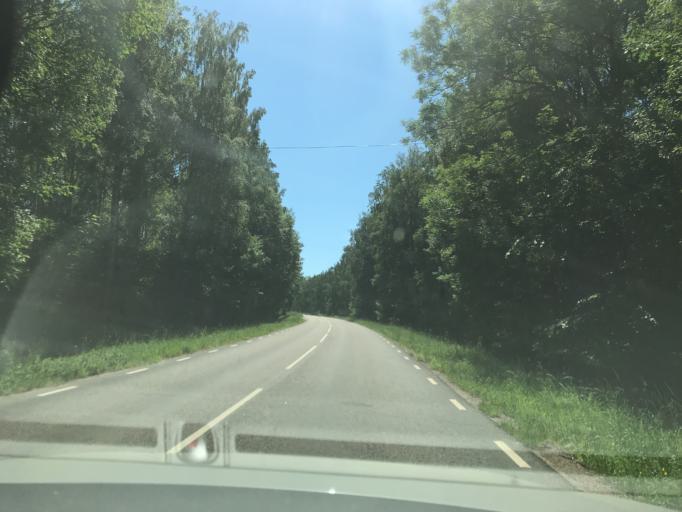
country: SE
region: Vaestra Goetaland
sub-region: Gotene Kommun
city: Goetene
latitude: 58.6201
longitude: 13.4049
